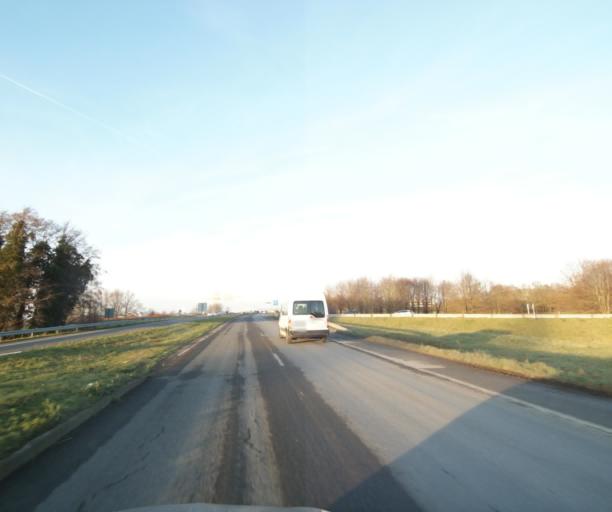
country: FR
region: Nord-Pas-de-Calais
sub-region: Departement du Nord
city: Famars
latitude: 50.3353
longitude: 3.5132
